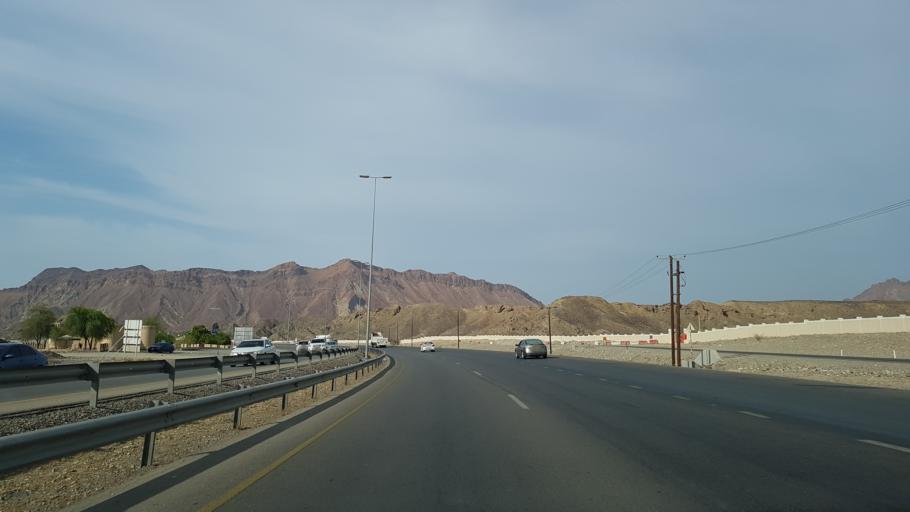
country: OM
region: Muhafazat ad Dakhiliyah
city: Bidbid
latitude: 23.4189
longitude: 58.1191
